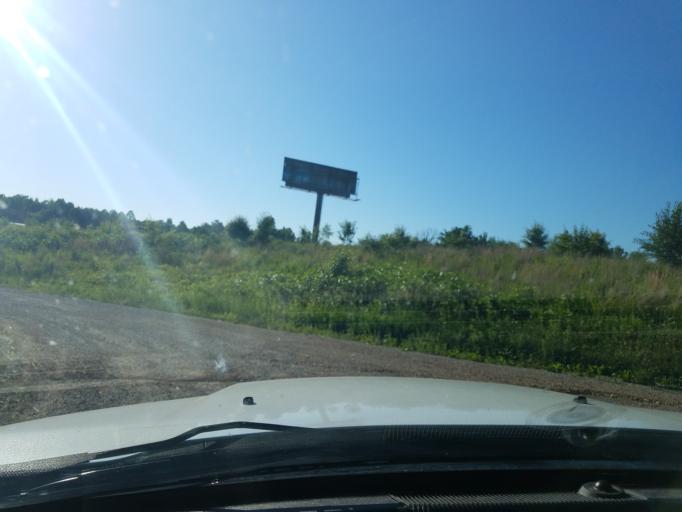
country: US
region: Tennessee
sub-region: Putnam County
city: Baxter
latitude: 36.1381
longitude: -85.5745
